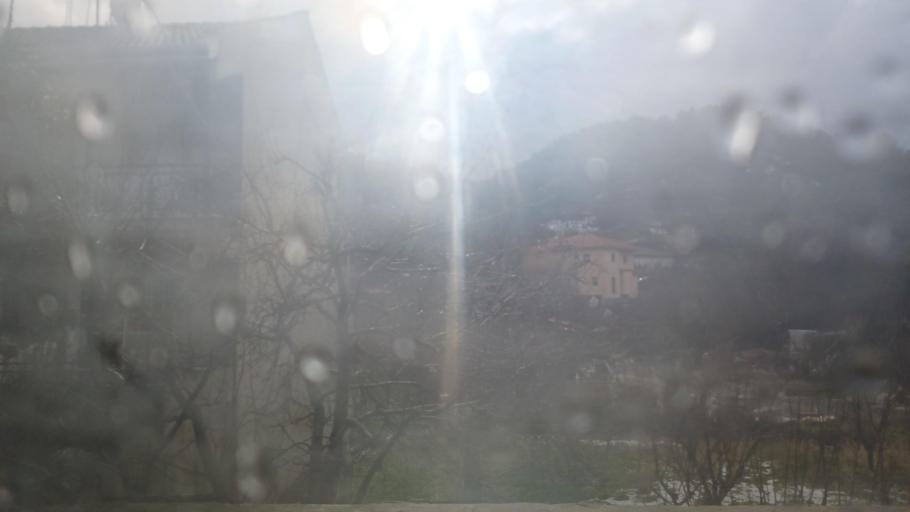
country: CY
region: Limassol
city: Kyperounta
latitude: 34.9410
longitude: 32.9617
